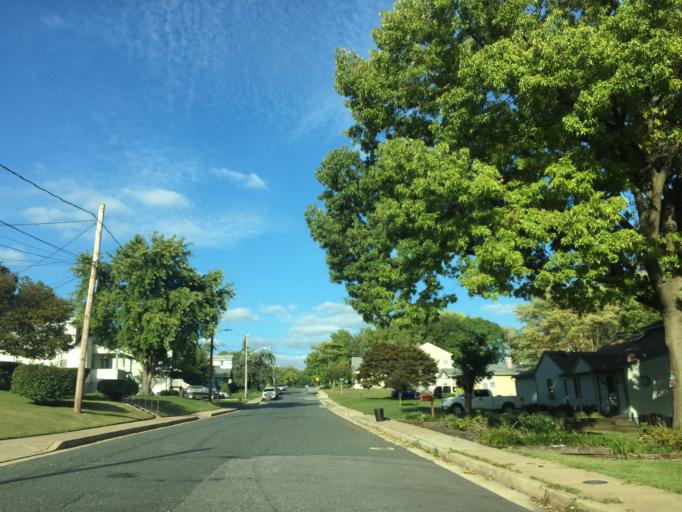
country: US
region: Maryland
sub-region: Baltimore County
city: Overlea
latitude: 39.3580
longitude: -76.5218
